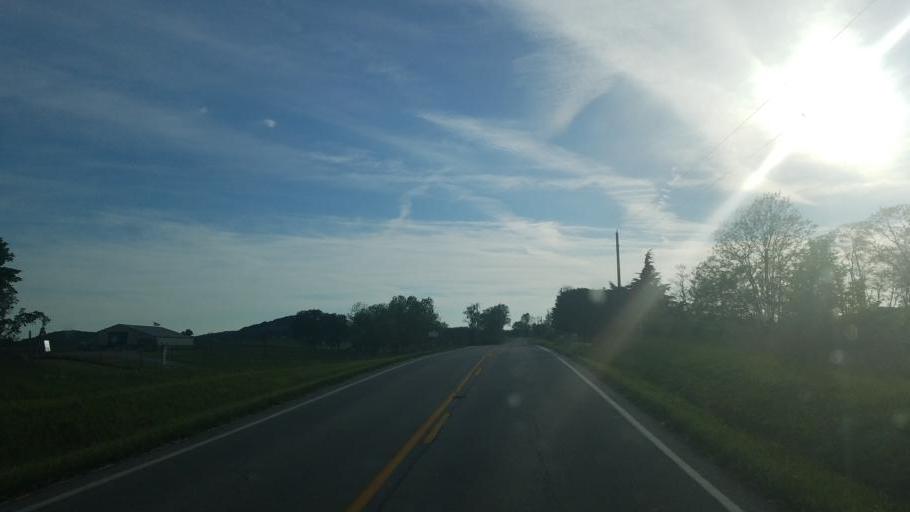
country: US
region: Ohio
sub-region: Ross County
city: Frankfort
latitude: 39.4239
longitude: -83.2573
